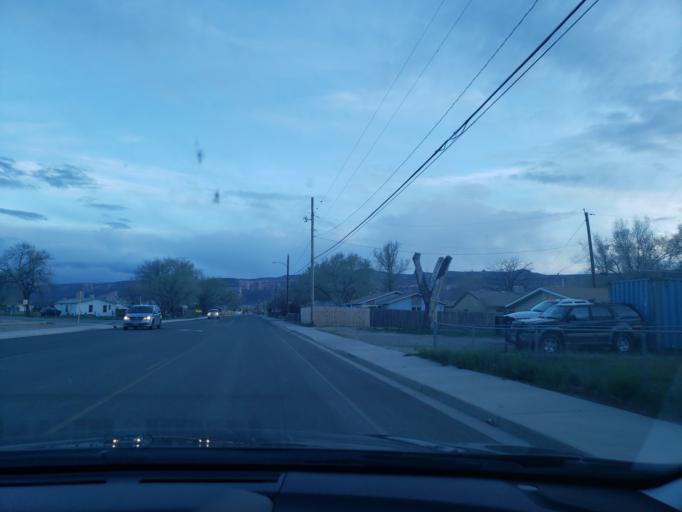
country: US
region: Colorado
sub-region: Mesa County
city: Fruita
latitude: 39.1553
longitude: -108.7198
